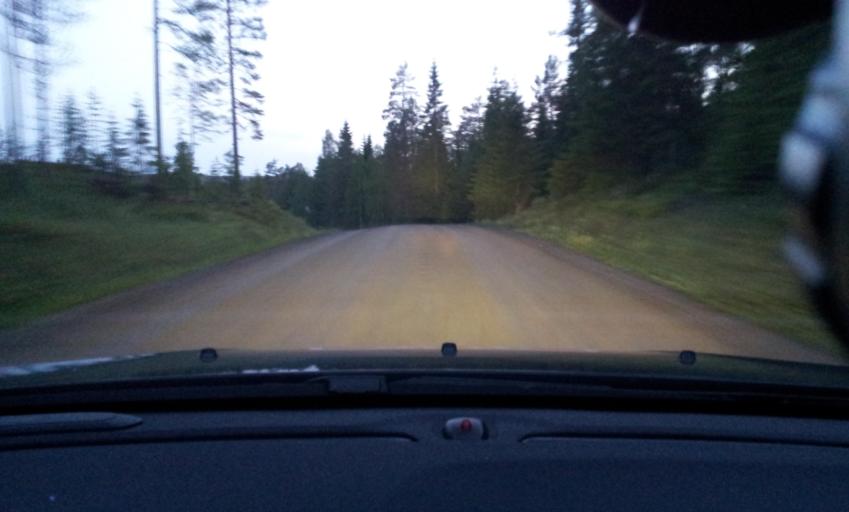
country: SE
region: Jaemtland
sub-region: Braecke Kommun
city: Braecke
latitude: 62.7177
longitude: 15.6138
